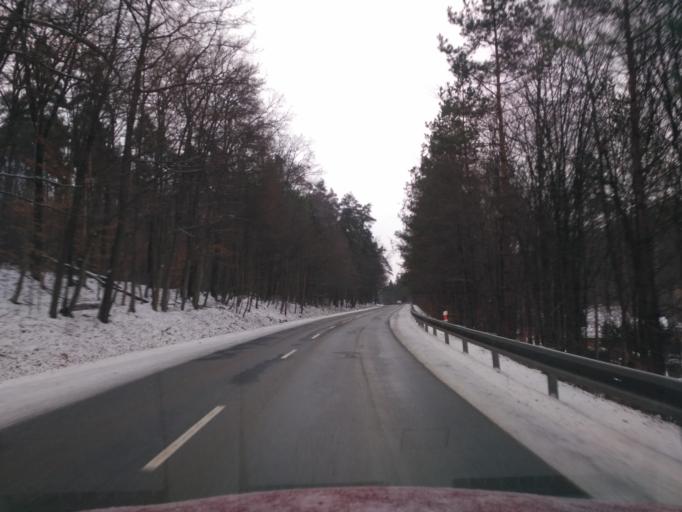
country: SK
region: Presovsky
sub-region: Okres Presov
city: Presov
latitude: 48.9716
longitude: 21.1688
